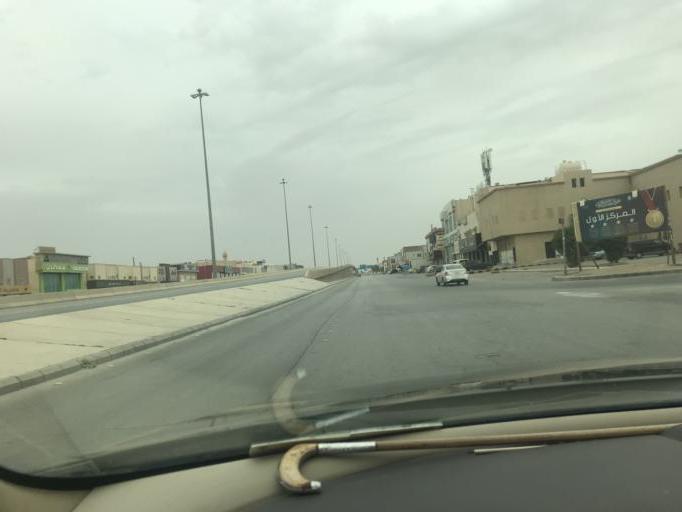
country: SA
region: Ar Riyad
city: Riyadh
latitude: 24.7940
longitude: 46.6996
